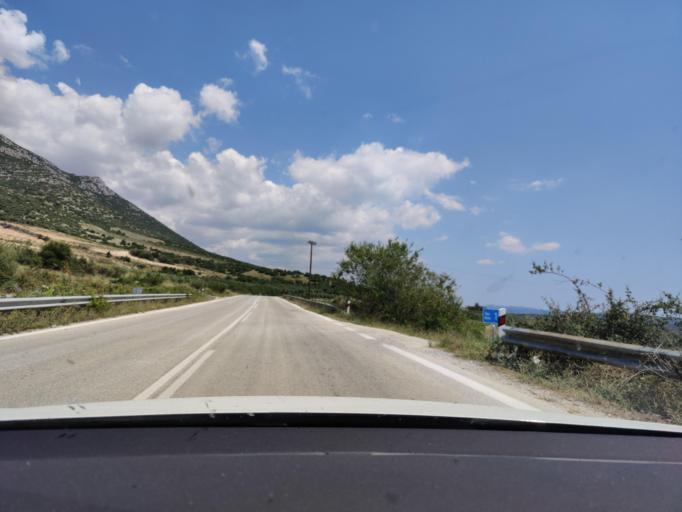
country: GR
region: East Macedonia and Thrace
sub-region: Nomos Kavalas
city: Paralia Ofryniou
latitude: 40.8036
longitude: 23.9622
